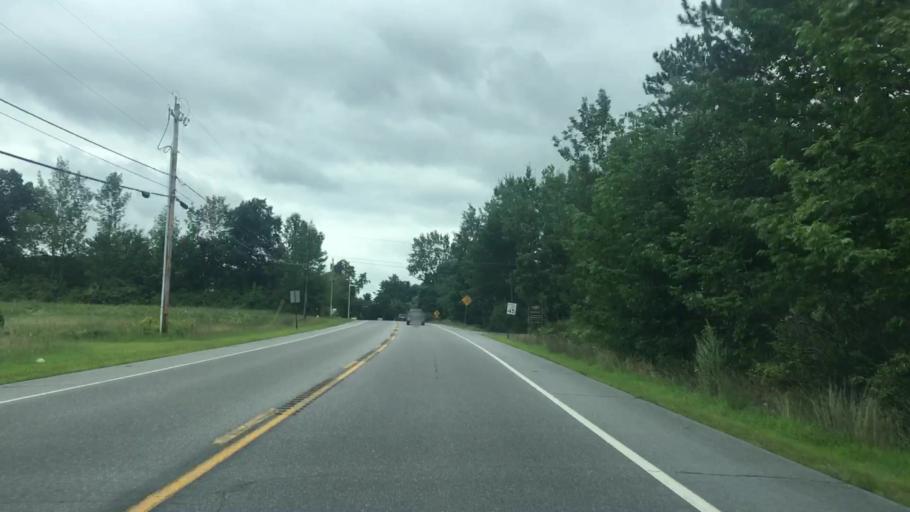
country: US
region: Maine
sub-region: York County
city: Alfred
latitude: 43.4907
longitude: -70.7199
